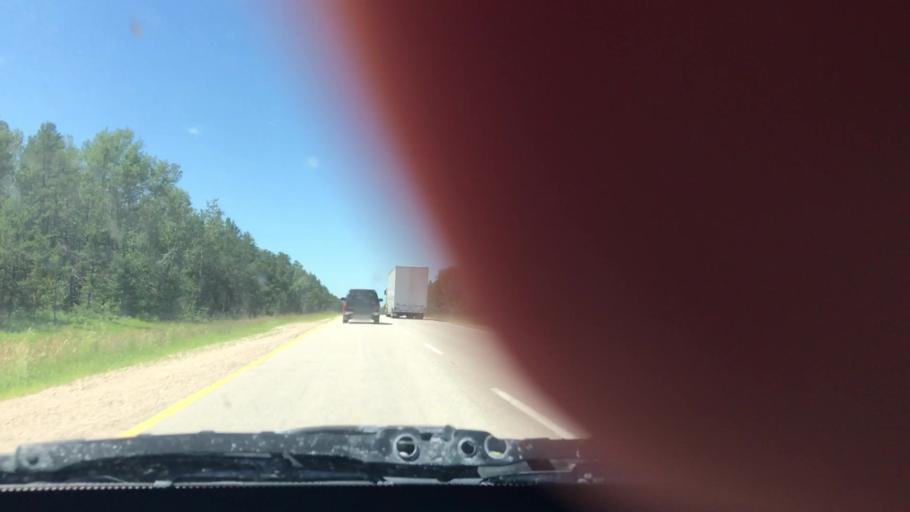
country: CA
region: Manitoba
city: La Broquerie
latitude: 49.6574
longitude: -96.1964
